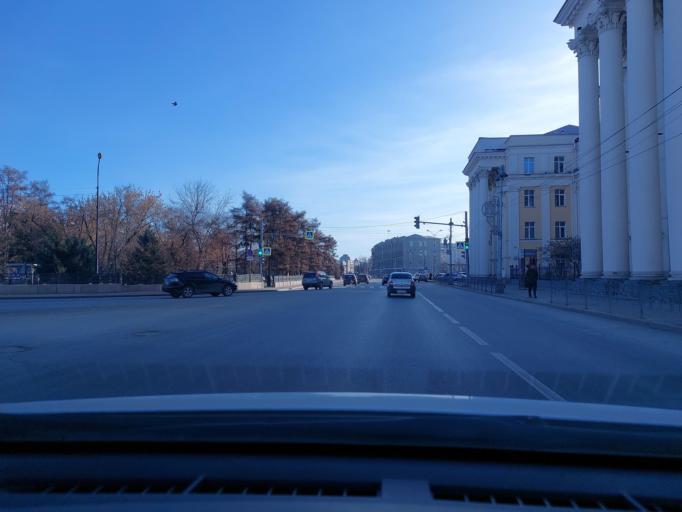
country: RU
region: Irkutsk
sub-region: Irkutskiy Rayon
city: Irkutsk
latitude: 52.2891
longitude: 104.2794
